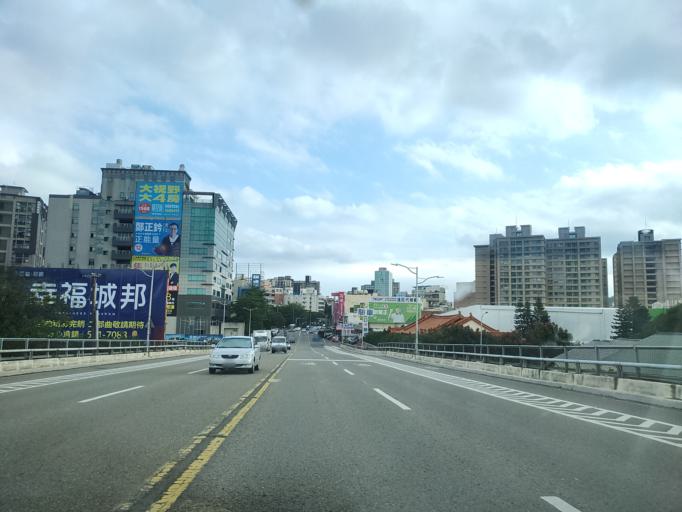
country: TW
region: Taiwan
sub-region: Hsinchu
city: Hsinchu
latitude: 24.8075
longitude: 120.9852
